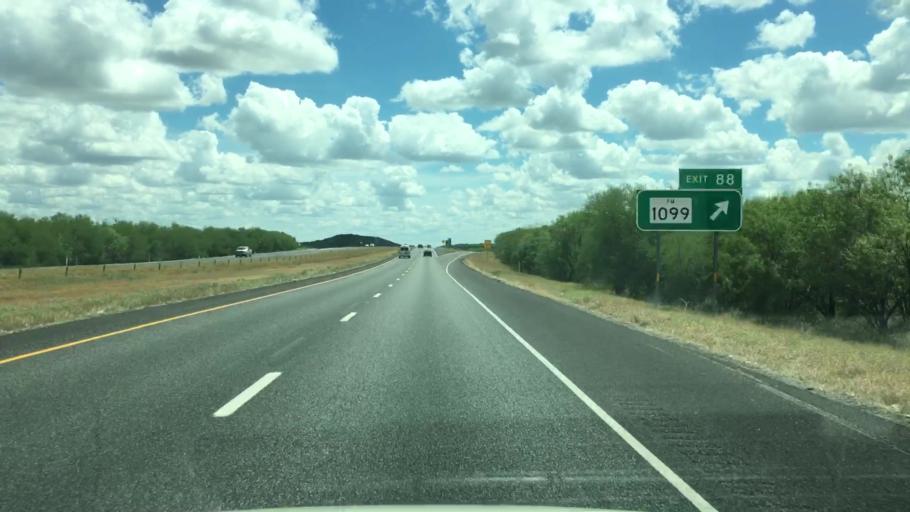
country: US
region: Texas
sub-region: Atascosa County
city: Pleasanton
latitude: 28.7394
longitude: -98.2914
